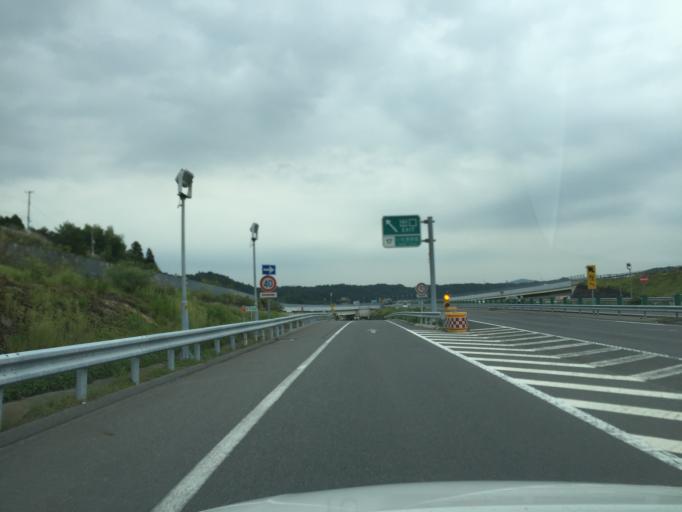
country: JP
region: Fukushima
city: Iwaki
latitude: 37.0651
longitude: 140.8354
